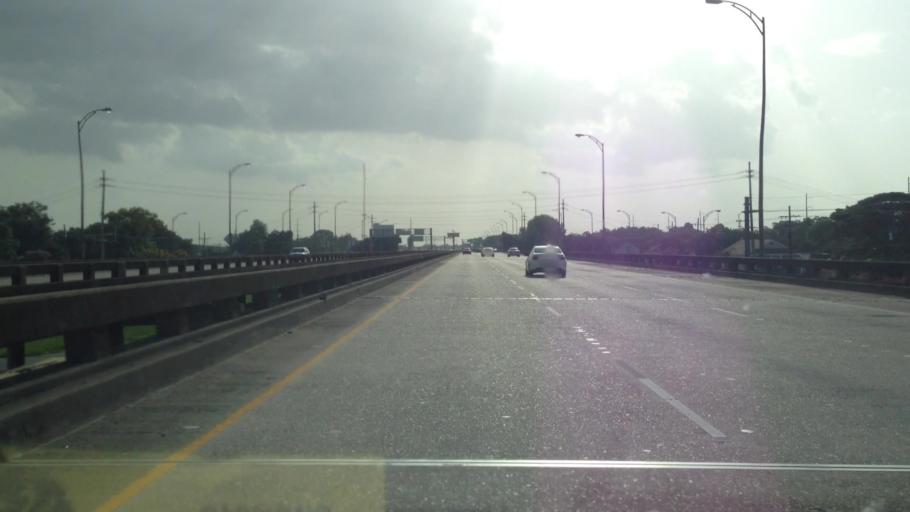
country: US
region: Louisiana
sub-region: Orleans Parish
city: New Orleans
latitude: 29.9915
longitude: -90.0580
